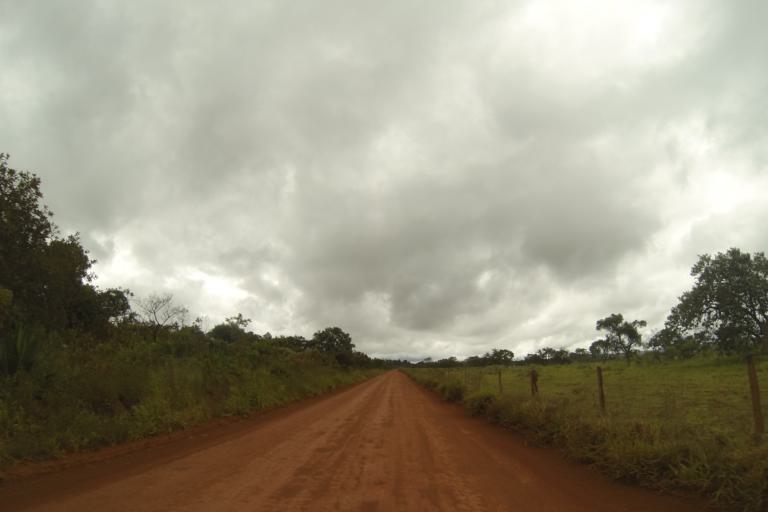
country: BR
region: Minas Gerais
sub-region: Campos Altos
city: Campos Altos
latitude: -19.8099
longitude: -46.3473
